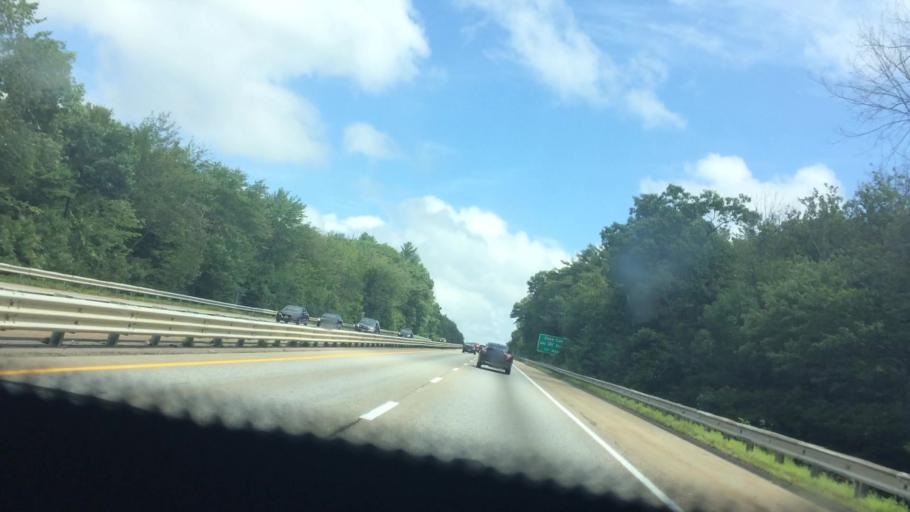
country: US
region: Massachusetts
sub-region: Worcester County
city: Harvard
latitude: 42.5259
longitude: -71.5428
